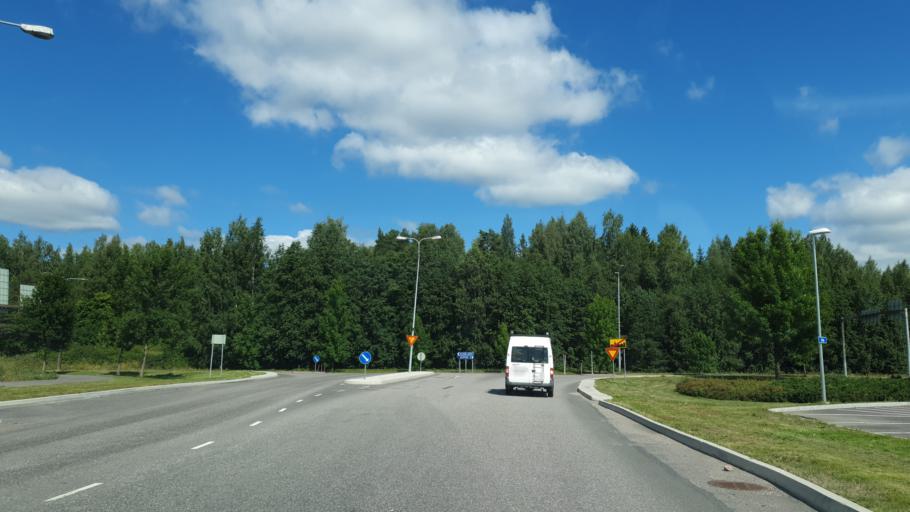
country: FI
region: Uusimaa
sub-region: Helsinki
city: Nurmijaervi
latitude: 60.4554
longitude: 24.8410
